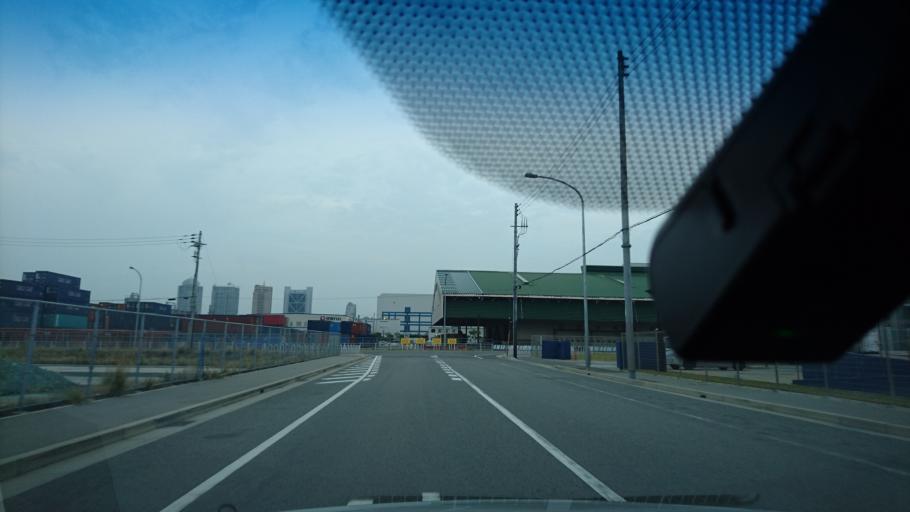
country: JP
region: Hyogo
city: Ashiya
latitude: 34.6863
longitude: 135.2550
